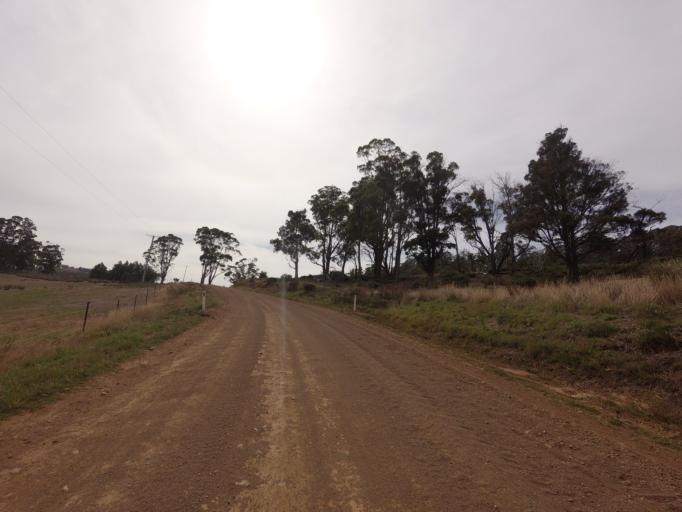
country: AU
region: Tasmania
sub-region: Sorell
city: Sorell
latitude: -42.4807
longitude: 147.5842
